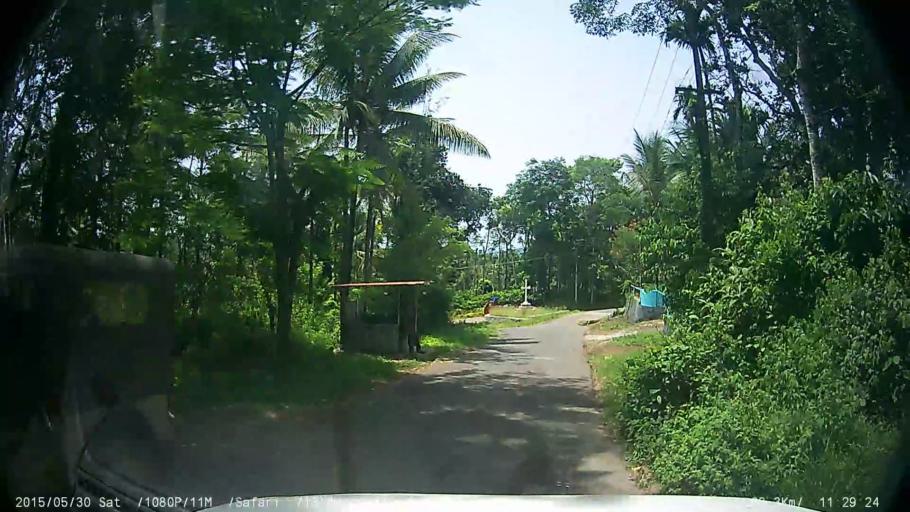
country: IN
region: Kerala
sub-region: Wayanad
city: Panamaram
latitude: 11.8095
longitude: 76.0494
